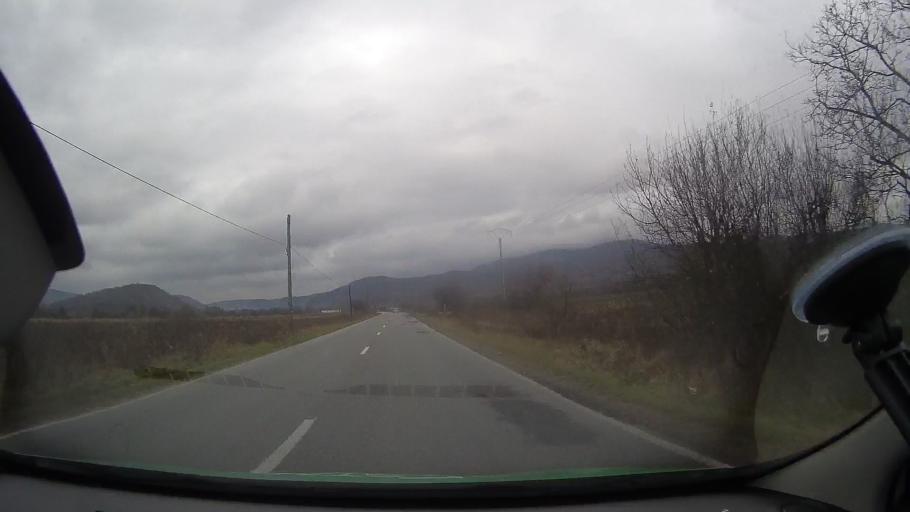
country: RO
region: Arad
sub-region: Comuna Buteni
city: Buteni
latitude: 46.3184
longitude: 22.1337
